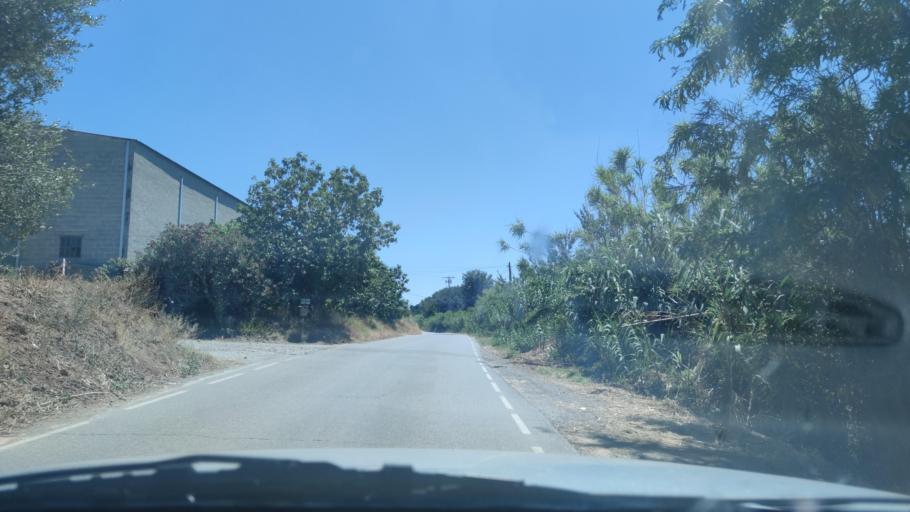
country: ES
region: Catalonia
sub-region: Provincia de Lleida
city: Lleida
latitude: 41.6311
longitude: 0.6561
